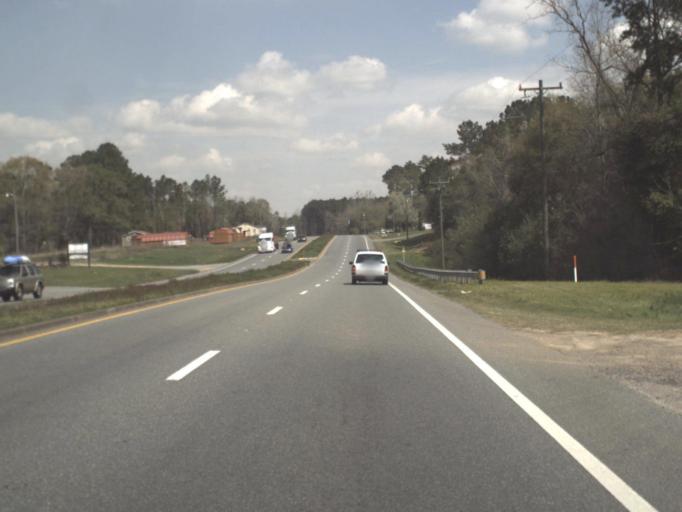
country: US
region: Florida
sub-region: Gadsden County
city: Havana
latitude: 30.6386
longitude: -84.4173
